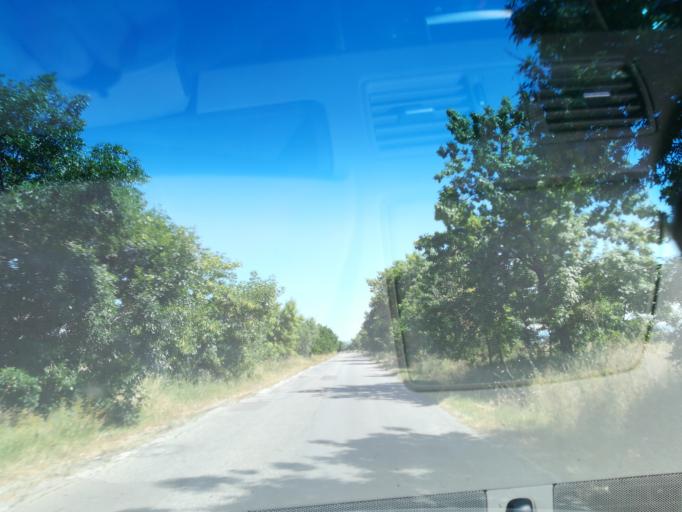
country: BG
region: Plovdiv
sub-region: Obshtina Sadovo
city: Sadovo
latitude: 42.0151
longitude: 25.0390
